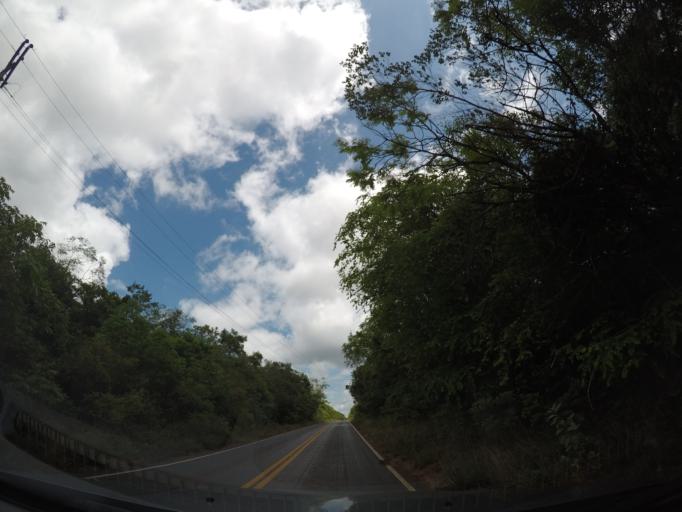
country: BR
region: Bahia
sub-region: Andarai
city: Vera Cruz
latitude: -12.5233
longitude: -41.3632
